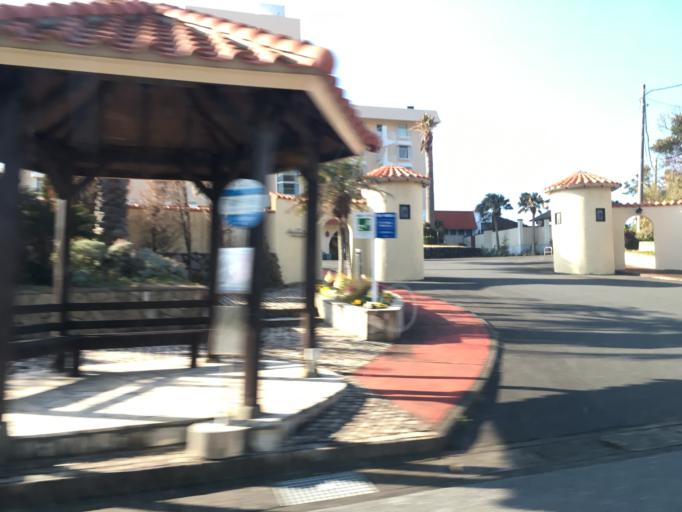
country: JP
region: Chiba
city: Tateyama
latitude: 34.9571
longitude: 139.7786
